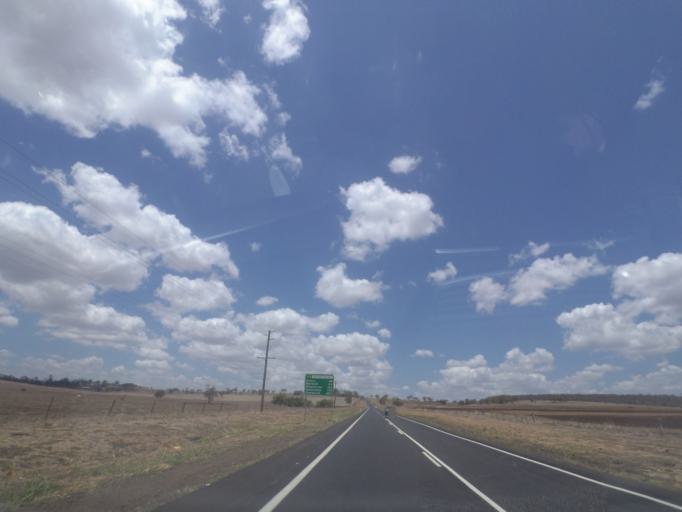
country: AU
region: Queensland
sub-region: Toowoomba
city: Top Camp
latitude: -27.7211
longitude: 151.9116
